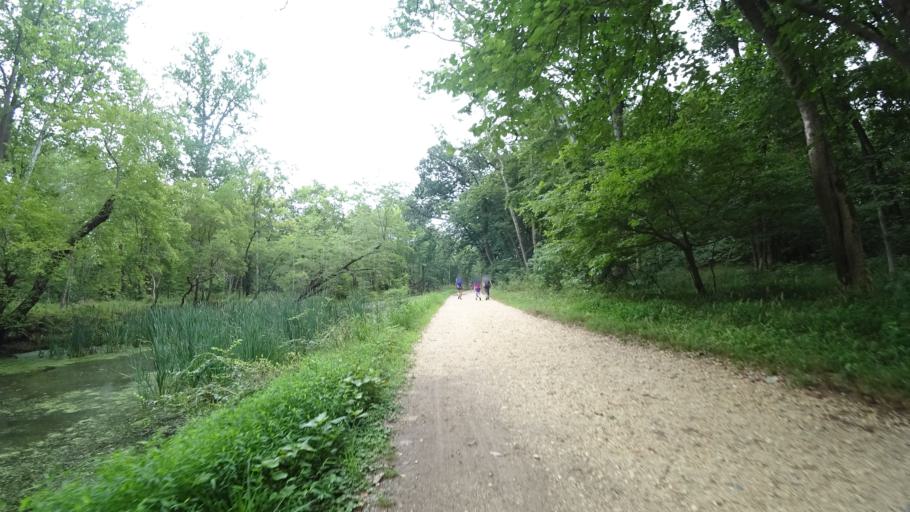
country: US
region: Maryland
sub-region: Montgomery County
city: Potomac
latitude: 38.9805
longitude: -77.2251
